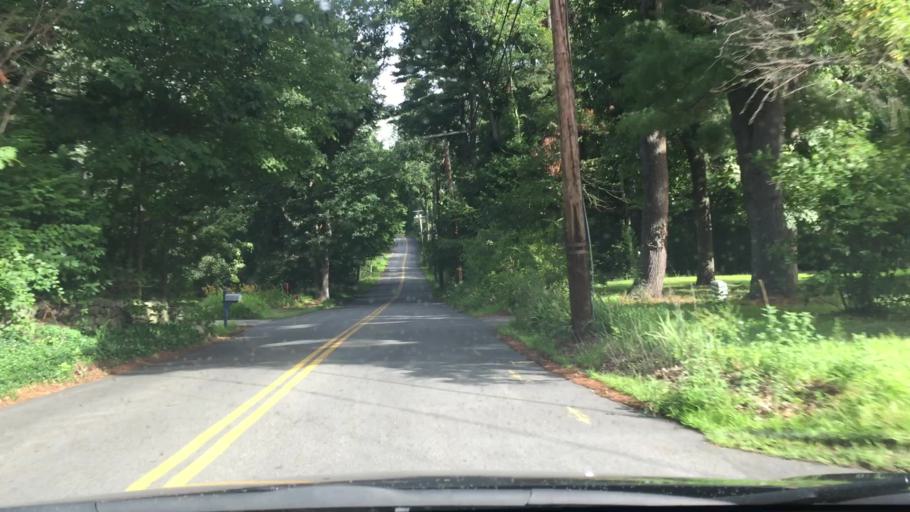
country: US
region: Massachusetts
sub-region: Middlesex County
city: Acton
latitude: 42.4910
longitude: -71.4337
